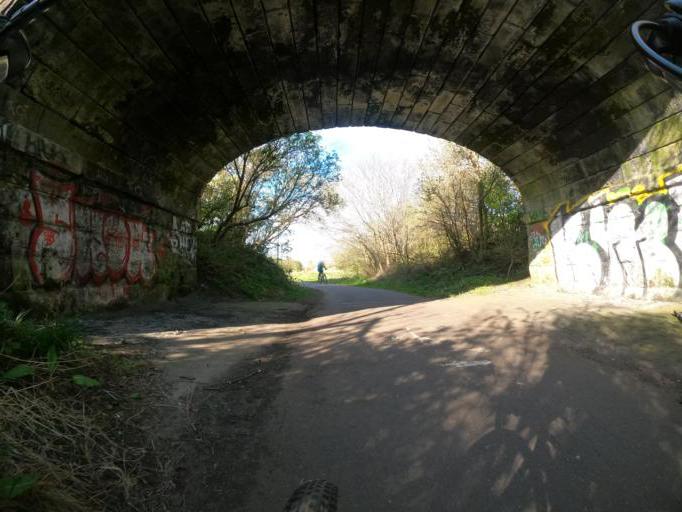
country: GB
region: Scotland
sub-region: Edinburgh
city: Edinburgh
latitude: 55.9636
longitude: -3.2420
